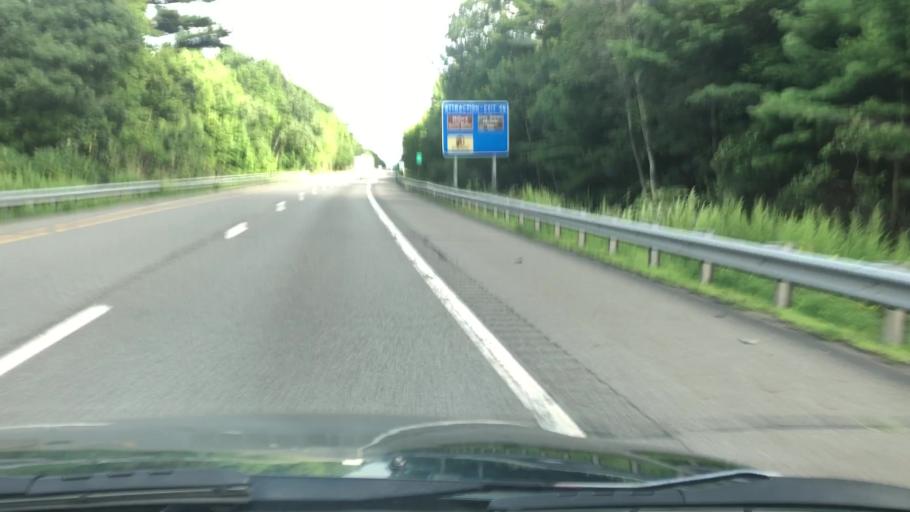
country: US
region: Pennsylvania
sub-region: Pike County
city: Milford
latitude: 41.3387
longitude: -74.8701
